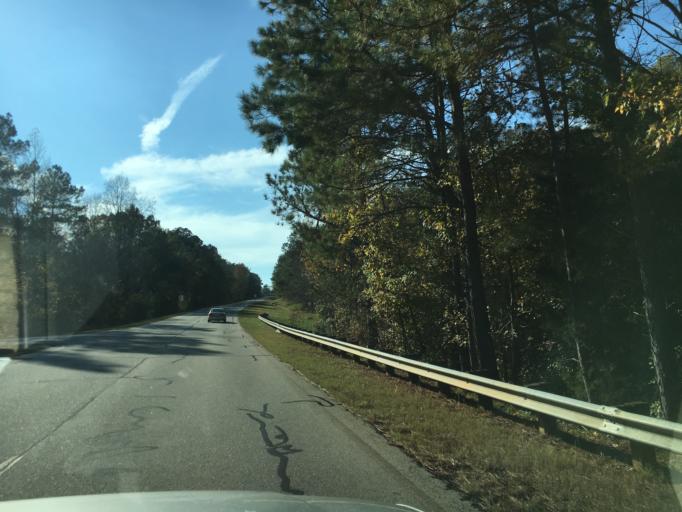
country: US
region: South Carolina
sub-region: Anderson County
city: Iva
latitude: 34.3240
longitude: -82.7935
